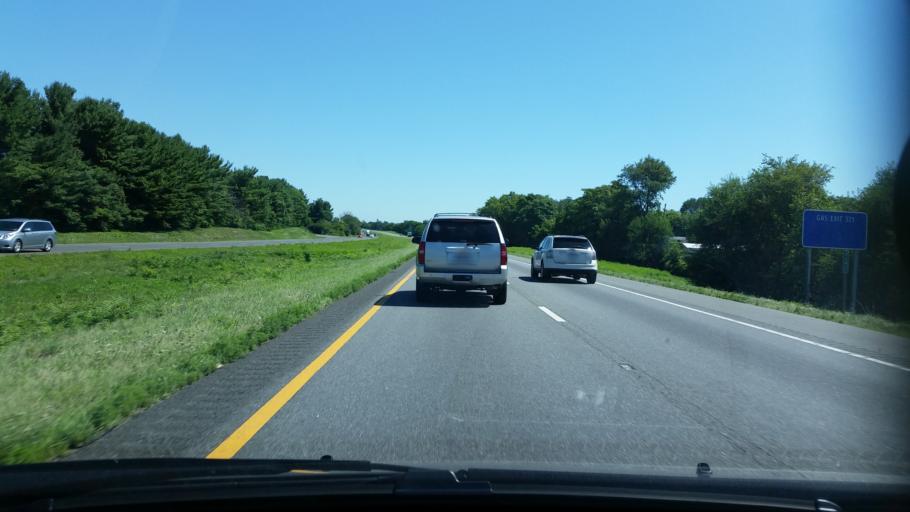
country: US
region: Virginia
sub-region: City of Winchester
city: Winchester
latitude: 39.2389
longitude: -78.1201
